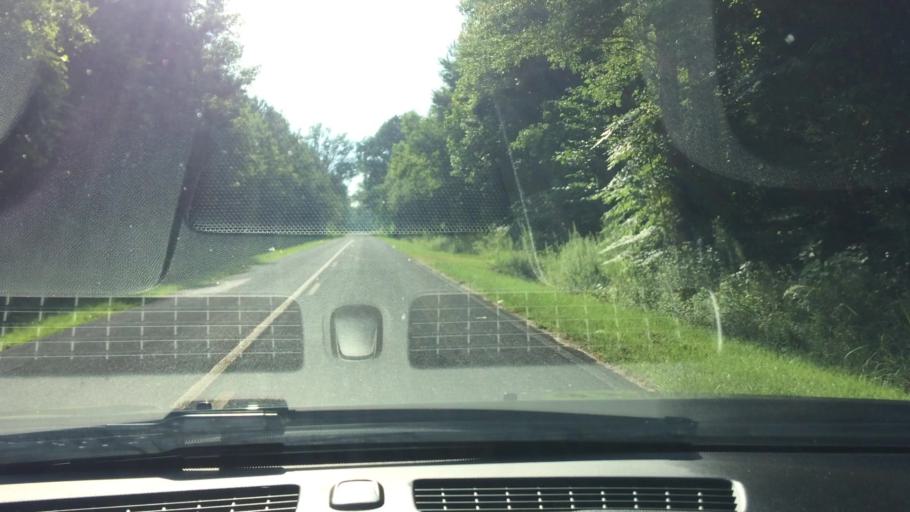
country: US
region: North Carolina
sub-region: Beaufort County
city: River Road
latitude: 35.4577
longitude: -77.0214
